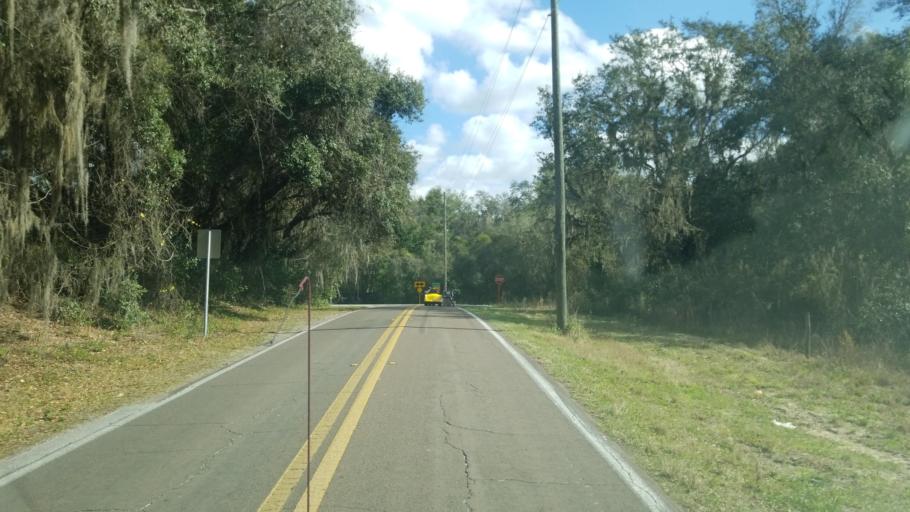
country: US
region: Florida
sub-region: Citrus County
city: Floral City
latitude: 28.7552
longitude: -82.2451
